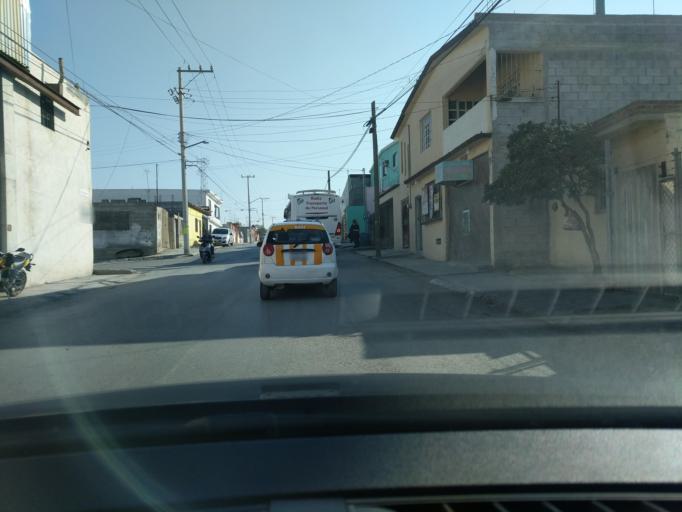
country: MX
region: Coahuila
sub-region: Ramos Arizpe
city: Ramos Arizpe
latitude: 25.5592
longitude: -100.9601
